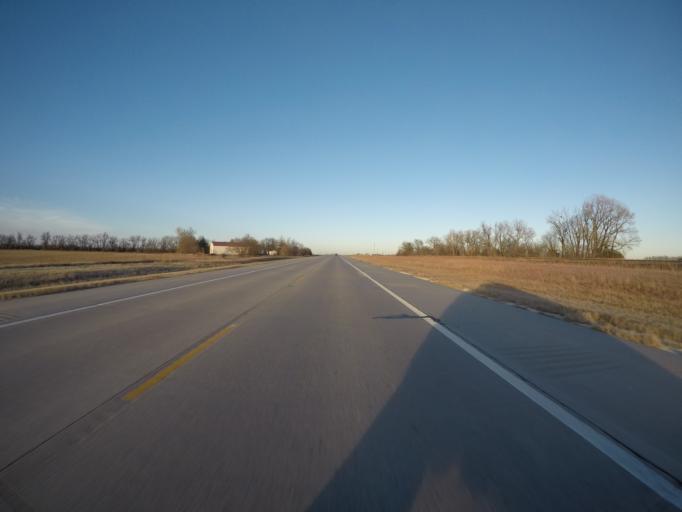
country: US
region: Kansas
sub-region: Harvey County
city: North Newton
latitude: 38.0837
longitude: -97.2918
